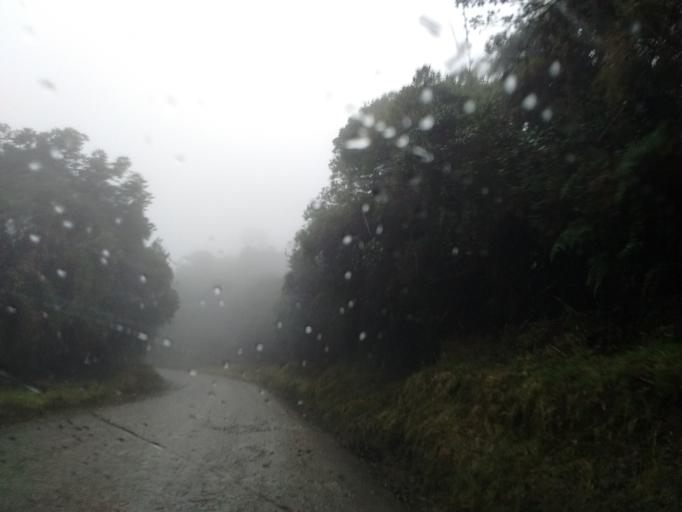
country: CO
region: Cauca
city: Paispamba
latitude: 2.1585
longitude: -76.4219
